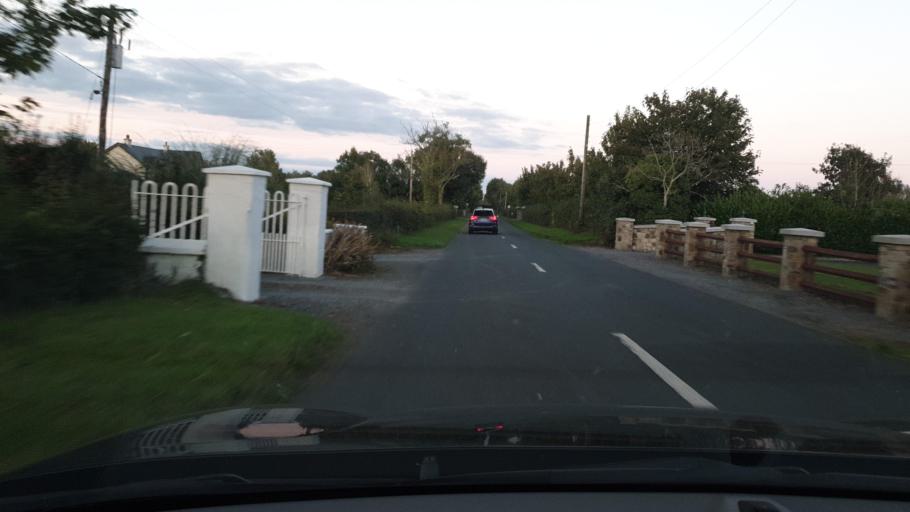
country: IE
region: Leinster
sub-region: Kildare
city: Clane
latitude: 53.3451
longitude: -6.6984
